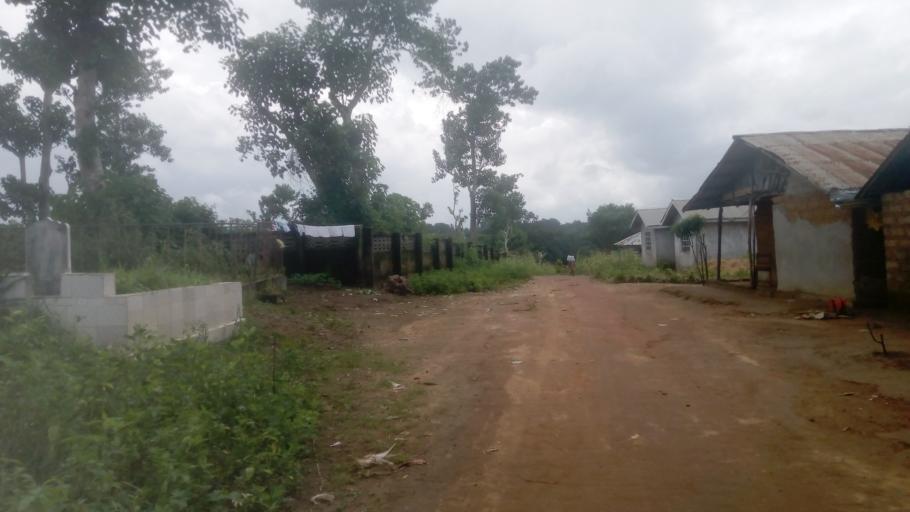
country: SL
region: Northern Province
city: Lunsar
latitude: 8.6953
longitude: -12.5388
